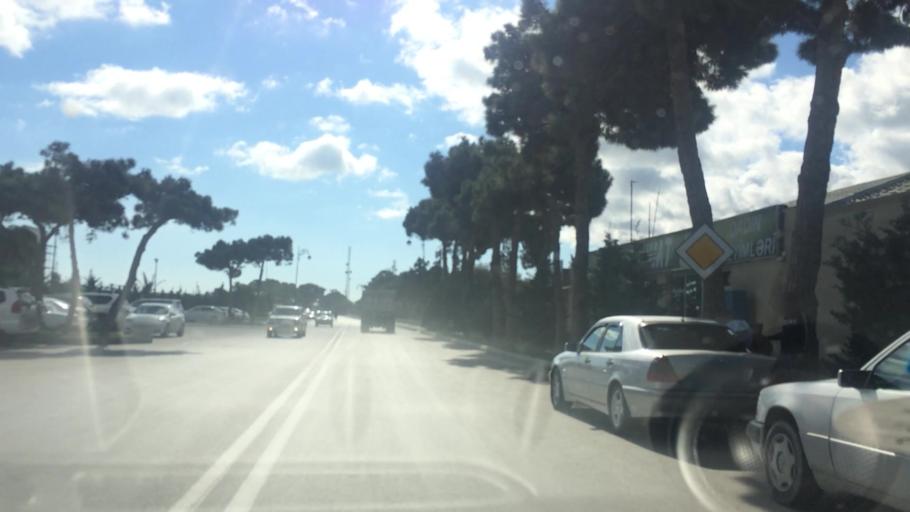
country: AZ
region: Baki
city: Pirallahi
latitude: 40.4680
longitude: 50.3264
